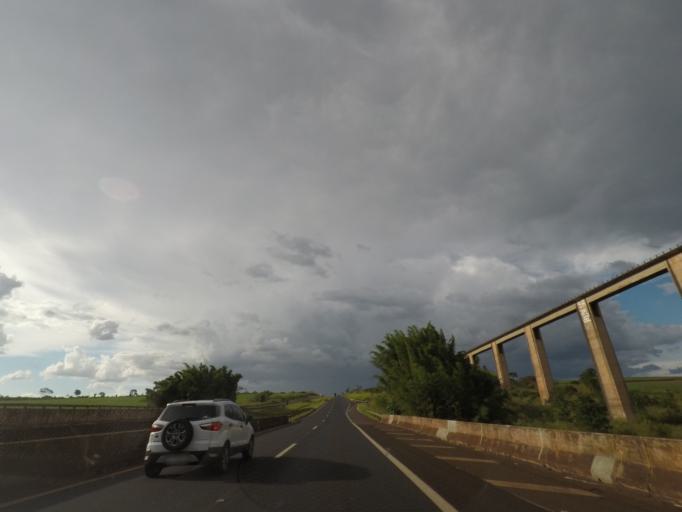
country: BR
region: Sao Paulo
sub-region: Jardinopolis
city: Jardinopolis
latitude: -21.0083
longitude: -47.8463
